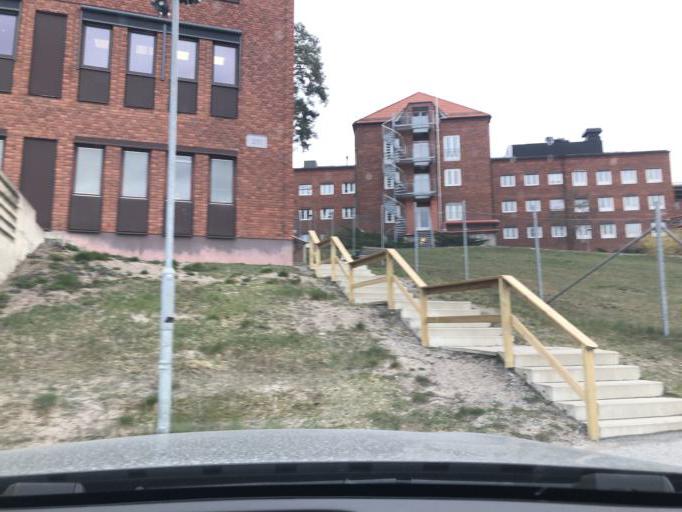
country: SE
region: Stockholm
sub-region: Sodertalje Kommun
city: Soedertaelje
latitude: 59.2035
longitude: 17.6138
